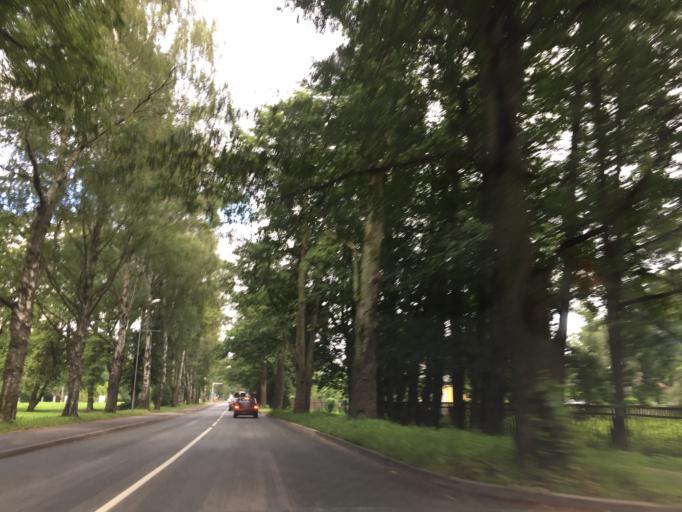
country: LV
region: Marupe
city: Marupe
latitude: 56.9523
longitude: 24.0204
